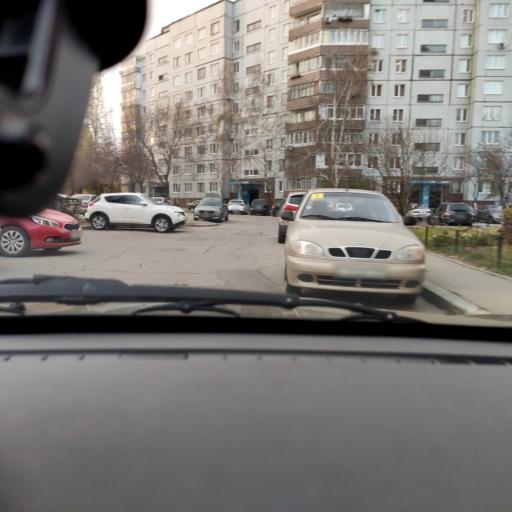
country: RU
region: Samara
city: Tol'yatti
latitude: 53.5405
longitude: 49.3165
